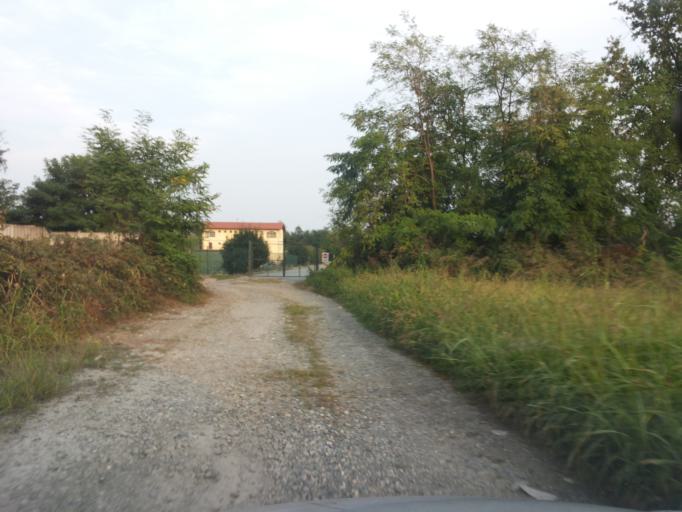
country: IT
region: Piedmont
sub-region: Provincia di Biella
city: Cavaglia
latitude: 45.3811
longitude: 8.1212
